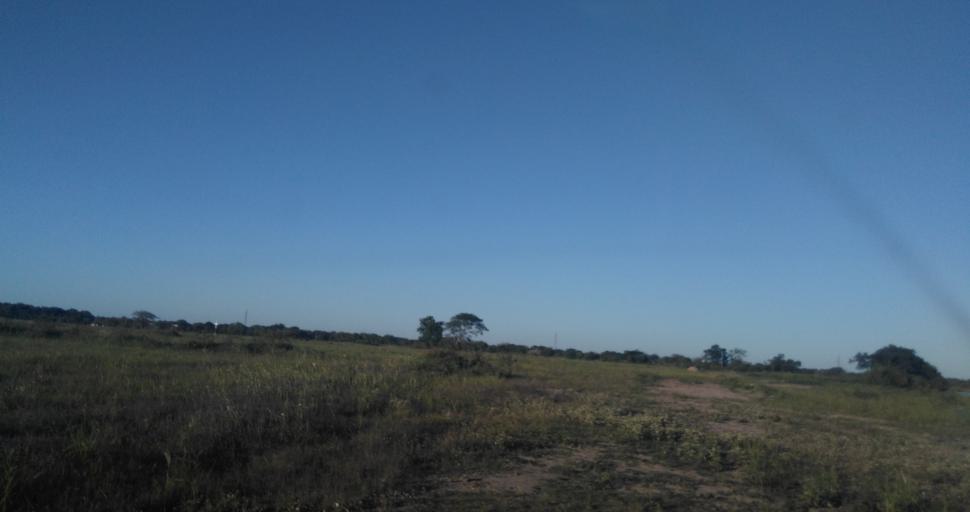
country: AR
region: Chaco
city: Fontana
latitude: -27.3949
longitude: -58.9834
